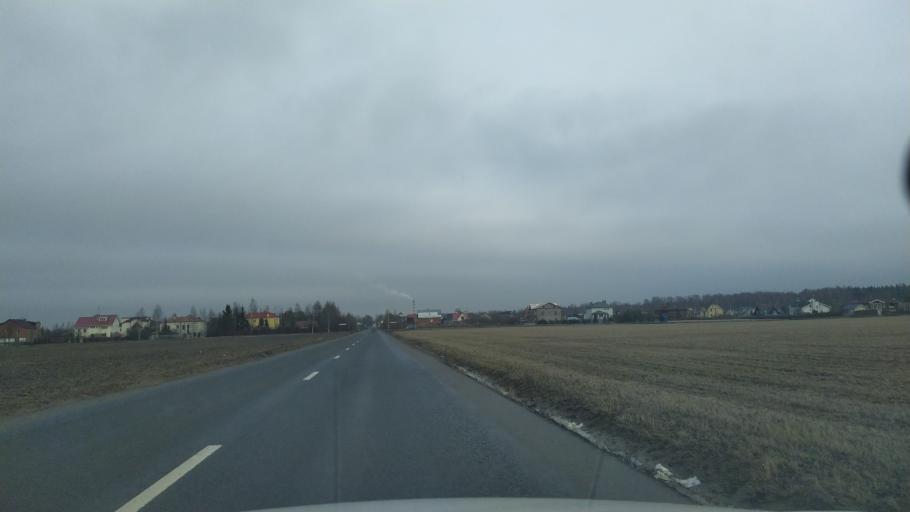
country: RU
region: St.-Petersburg
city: Aleksandrovskaya
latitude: 59.7203
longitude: 30.3432
